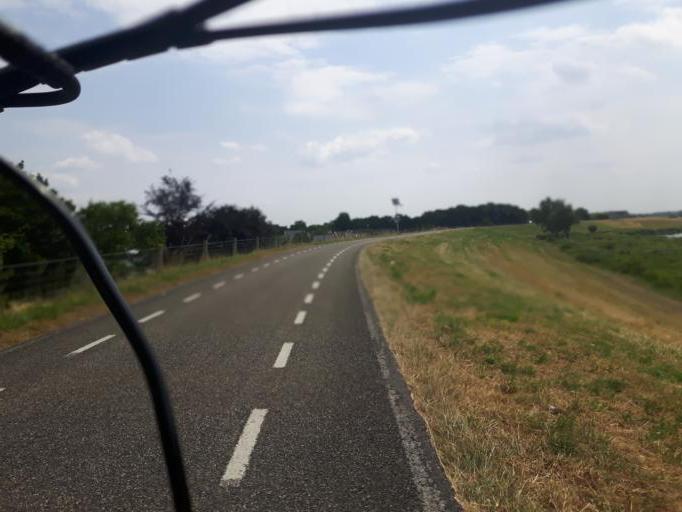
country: NL
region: Gelderland
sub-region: Gemeente Zaltbommel
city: Zaltbommel
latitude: 51.8221
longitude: 5.2041
